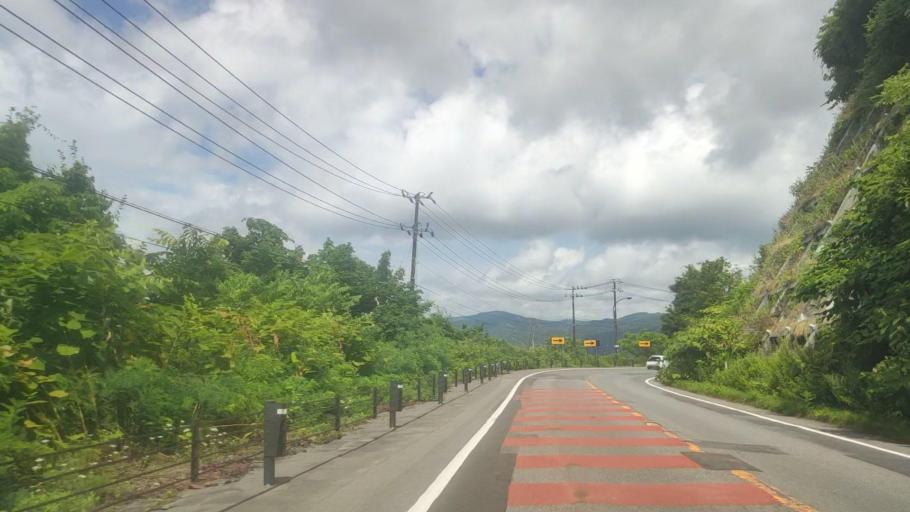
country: JP
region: Hokkaido
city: Date
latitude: 42.5646
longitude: 140.8802
